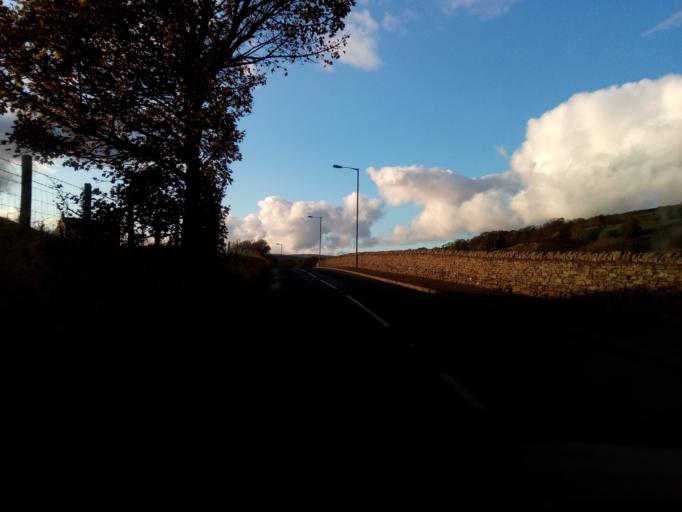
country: GB
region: England
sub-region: County Durham
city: Newbiggin
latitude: 54.7398
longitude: -2.1906
